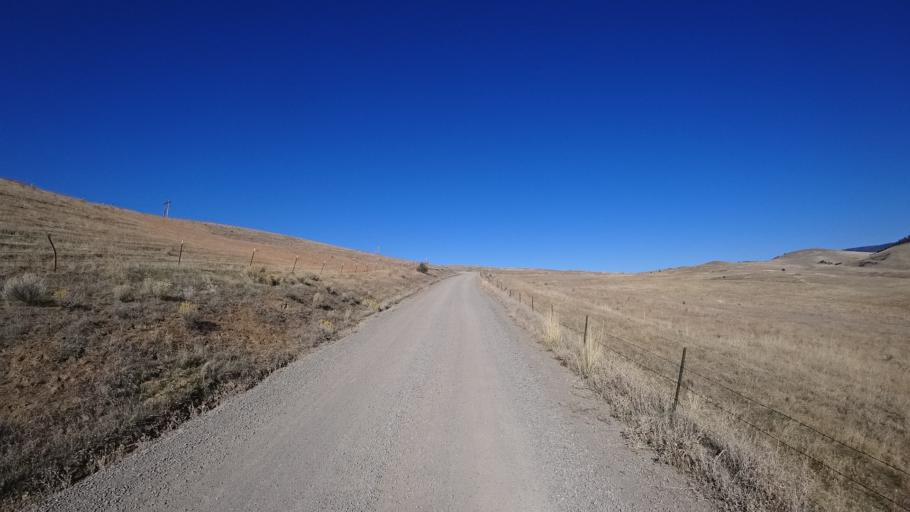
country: US
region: California
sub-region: Siskiyou County
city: Montague
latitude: 41.7661
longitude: -122.3570
